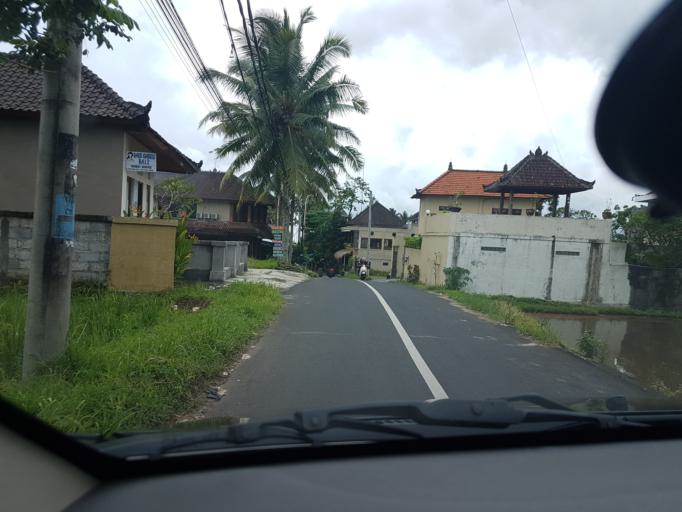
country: ID
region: Bali
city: Banjar Triwangsakeliki
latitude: -8.4667
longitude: 115.2721
